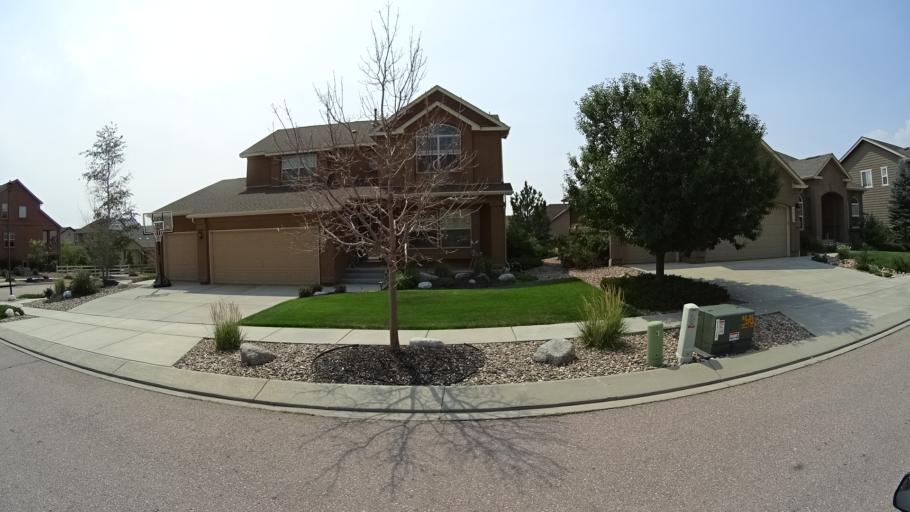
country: US
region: Colorado
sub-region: El Paso County
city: Black Forest
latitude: 38.9663
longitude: -104.7176
